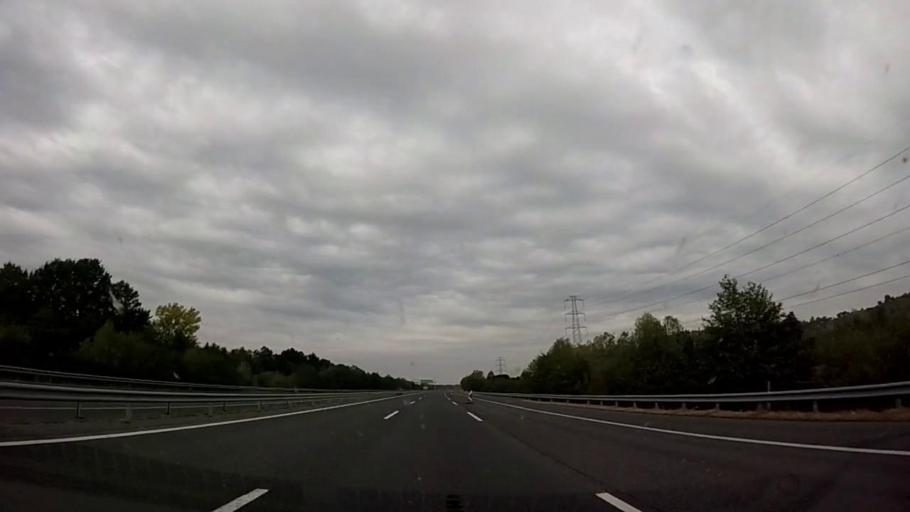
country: HR
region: Medimurska
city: Podturen
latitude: 46.5120
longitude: 16.5476
